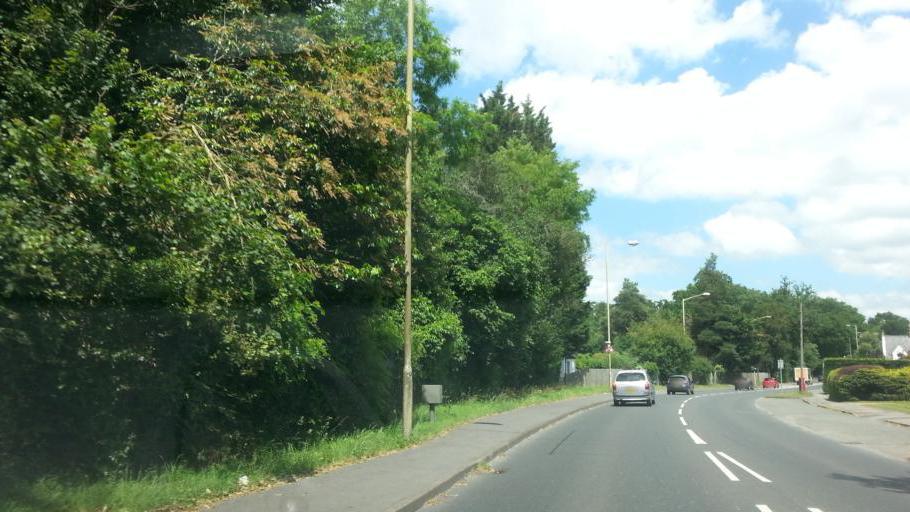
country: GB
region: England
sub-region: Wokingham
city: Earley
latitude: 51.4360
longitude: -0.9373
